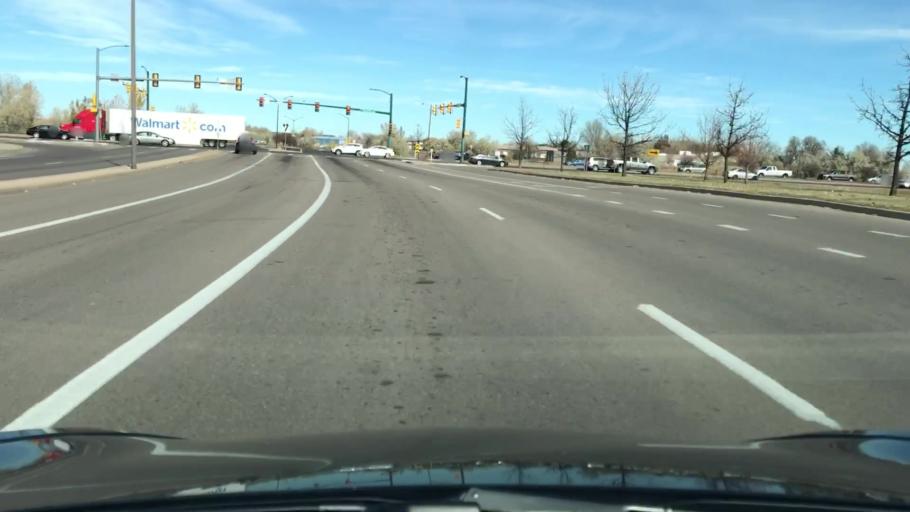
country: US
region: Colorado
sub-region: Larimer County
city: Fort Collins
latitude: 40.5801
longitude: -105.0326
